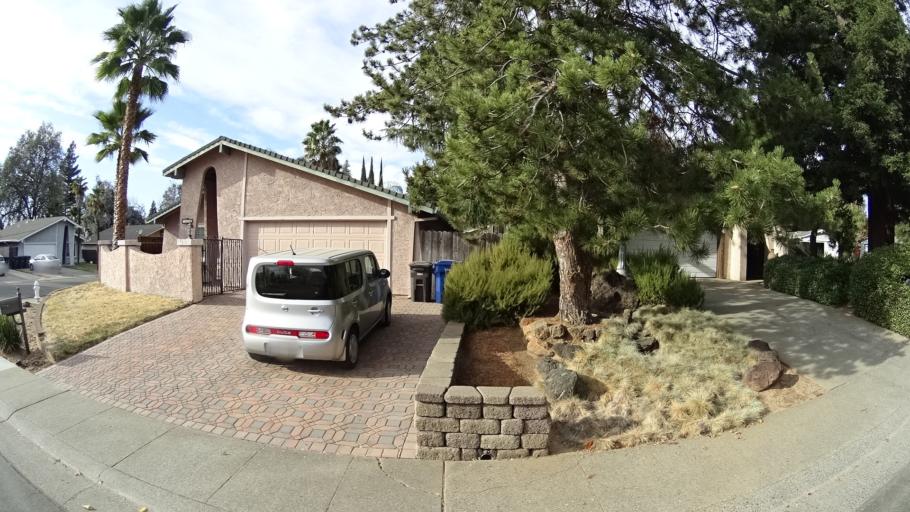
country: US
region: California
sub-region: Sacramento County
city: Citrus Heights
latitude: 38.7072
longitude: -121.2570
